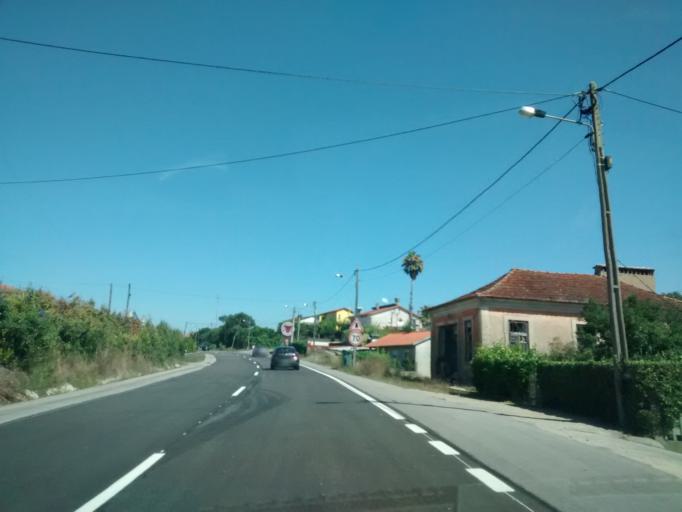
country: PT
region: Aveiro
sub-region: Oliveira do Bairro
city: Oliveira do Bairro
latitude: 40.5316
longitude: -8.5086
